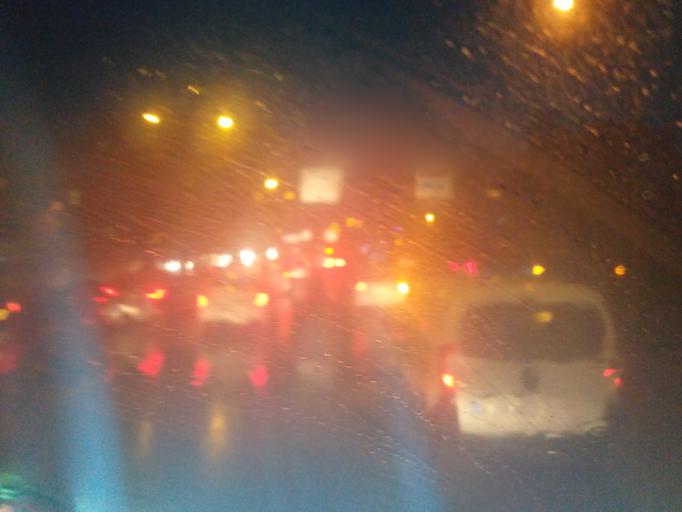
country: TR
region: Ankara
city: Ankara
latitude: 39.9548
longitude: 32.8202
